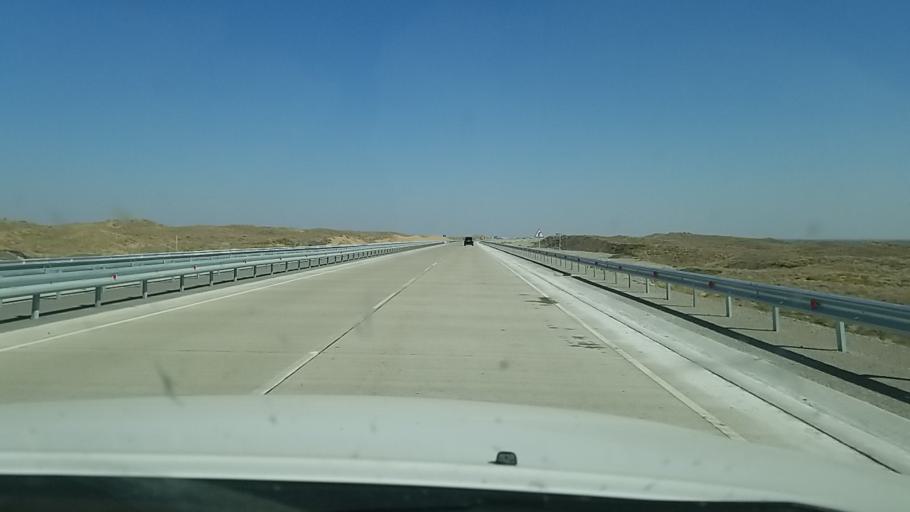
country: KZ
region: Almaty Oblysy
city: Zharkent
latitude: 44.1741
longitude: 80.3295
